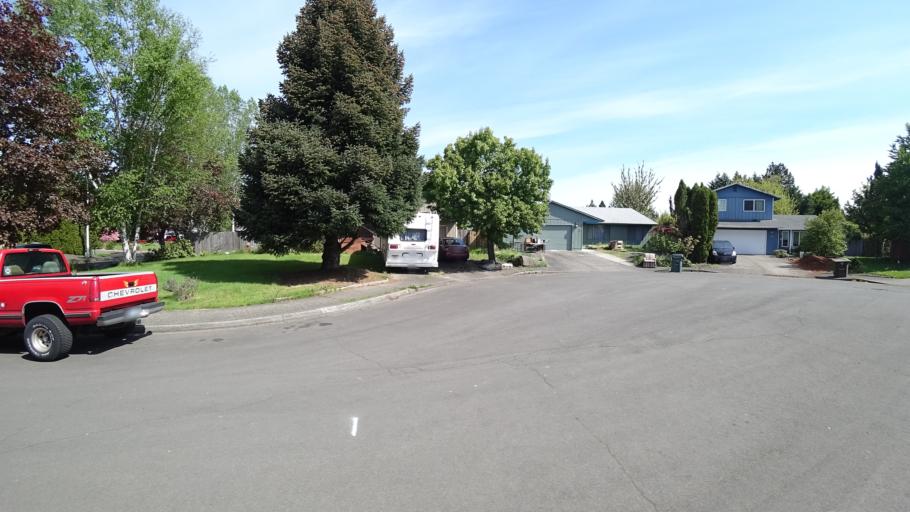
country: US
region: Oregon
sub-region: Washington County
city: Hillsboro
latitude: 45.5217
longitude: -122.9429
